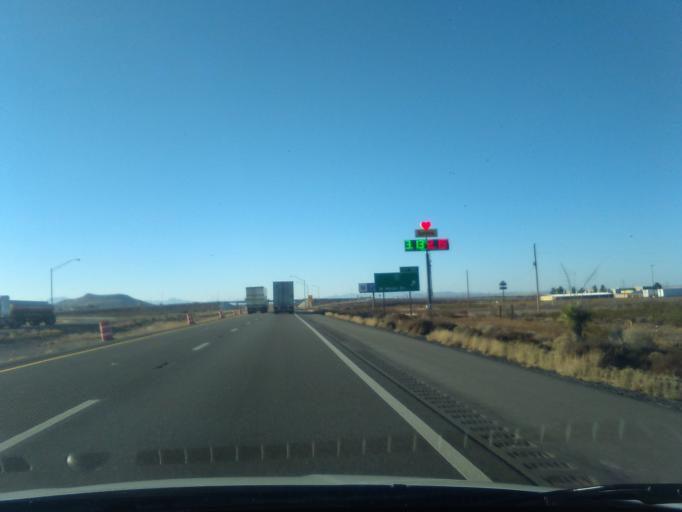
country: US
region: New Mexico
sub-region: Hidalgo County
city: Lordsburg
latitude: 32.3506
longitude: -108.7345
